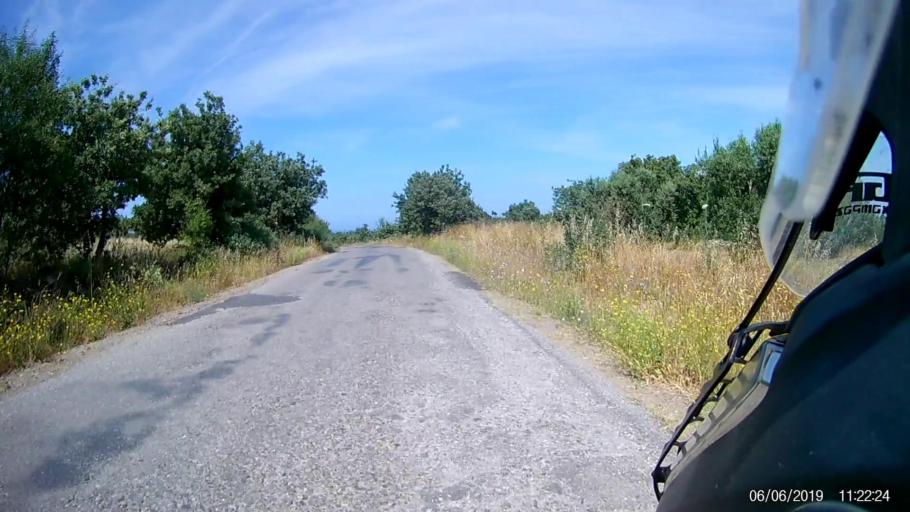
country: TR
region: Canakkale
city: Gulpinar
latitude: 39.6106
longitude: 26.1864
